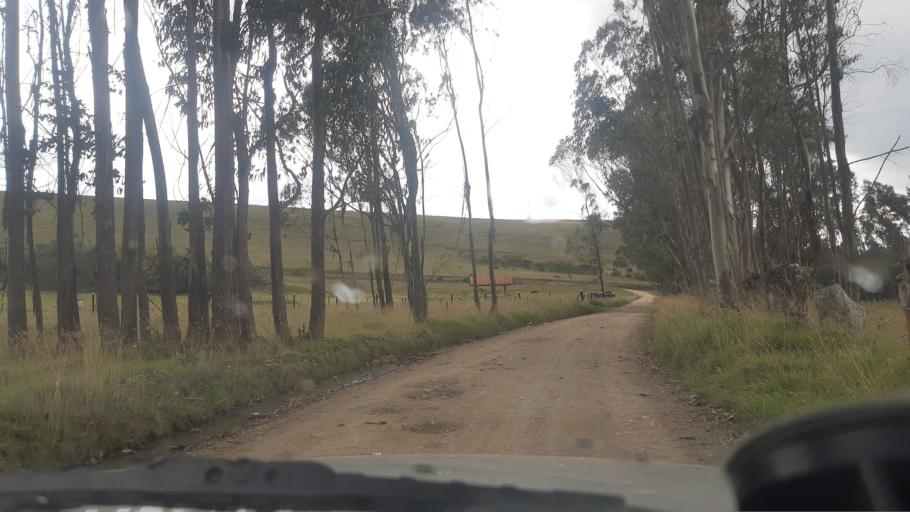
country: CO
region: Cundinamarca
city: Suesca
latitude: 5.1734
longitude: -73.8028
